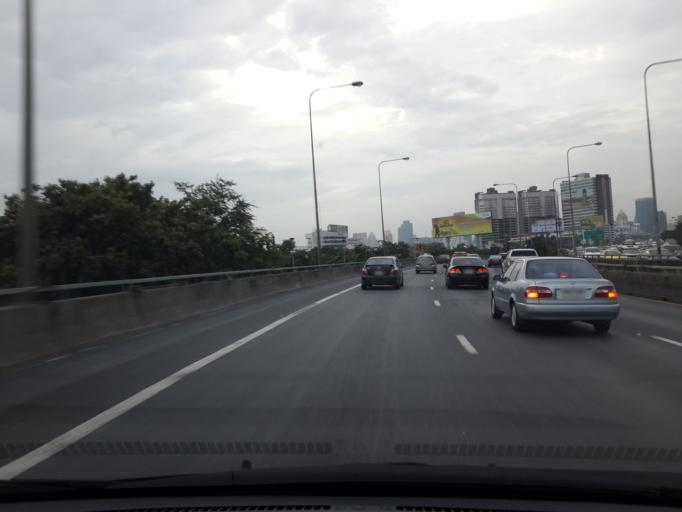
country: TH
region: Bangkok
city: Khlong Toei
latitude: 13.7112
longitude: 100.5637
